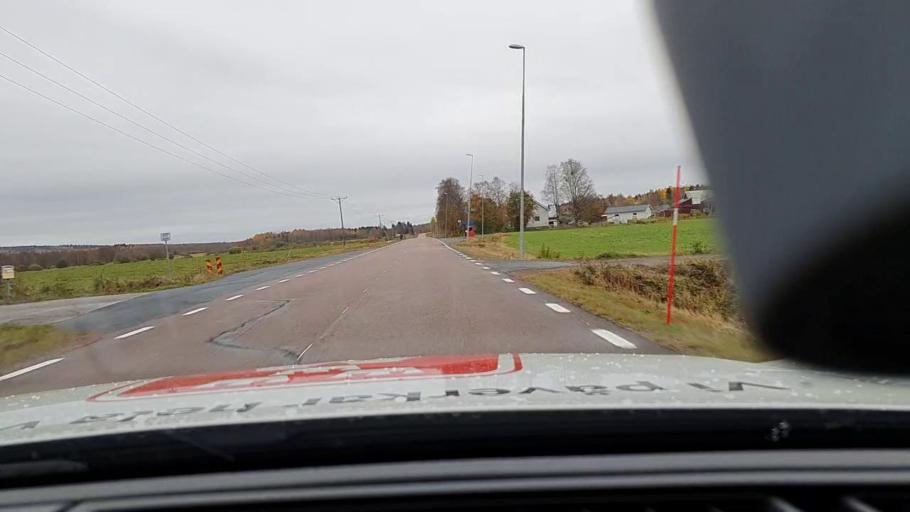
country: FI
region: Lapland
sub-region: Torniolaakso
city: Ylitornio
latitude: 66.1353
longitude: 23.9042
